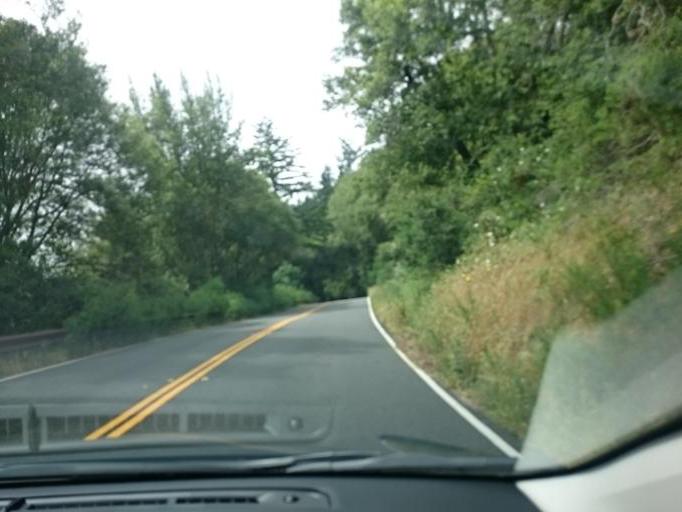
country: US
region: California
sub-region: Marin County
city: Lagunitas-Forest Knolls
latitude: 37.9851
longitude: -122.7420
